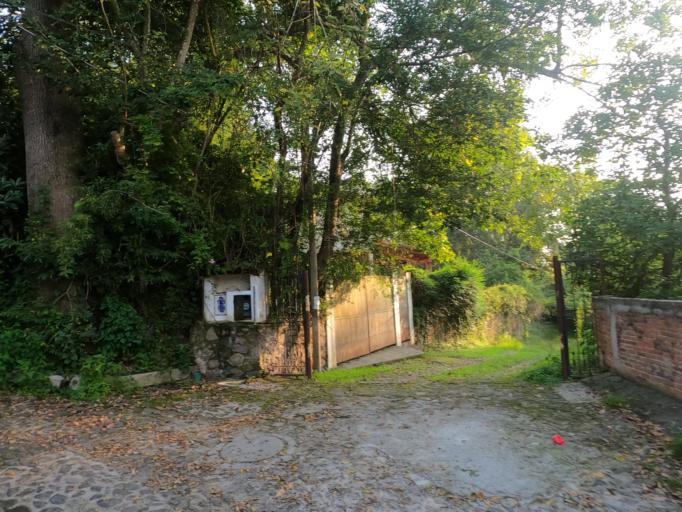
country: MX
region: Mexico
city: Valle de Bravo
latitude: 19.1962
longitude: -100.1277
